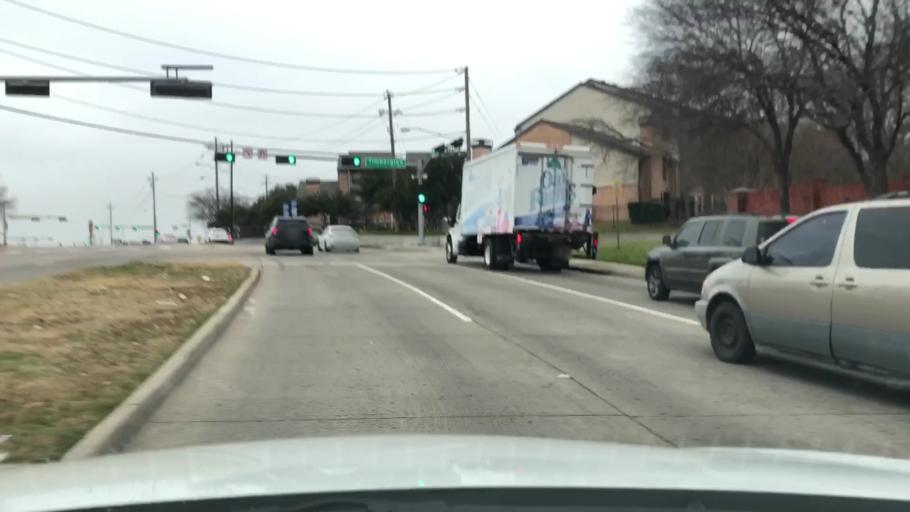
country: US
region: Texas
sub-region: Dallas County
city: Addison
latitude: 32.9990
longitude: -96.8557
